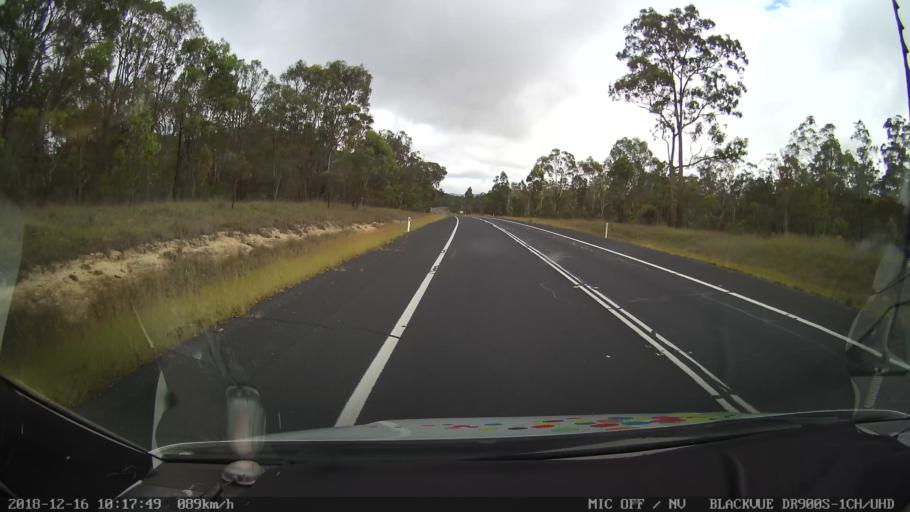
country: AU
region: New South Wales
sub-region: Tenterfield Municipality
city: Carrolls Creek
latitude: -29.2518
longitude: 151.9946
